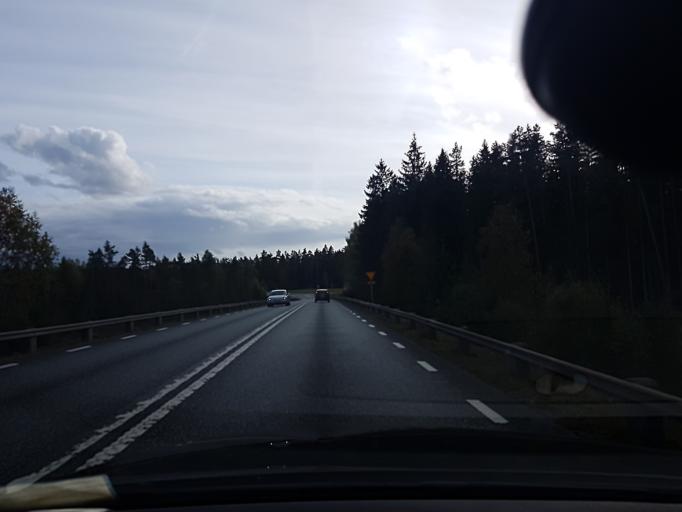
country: SE
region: Joenkoeping
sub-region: Varnamo Kommun
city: Bredaryd
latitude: 57.1716
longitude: 13.7638
